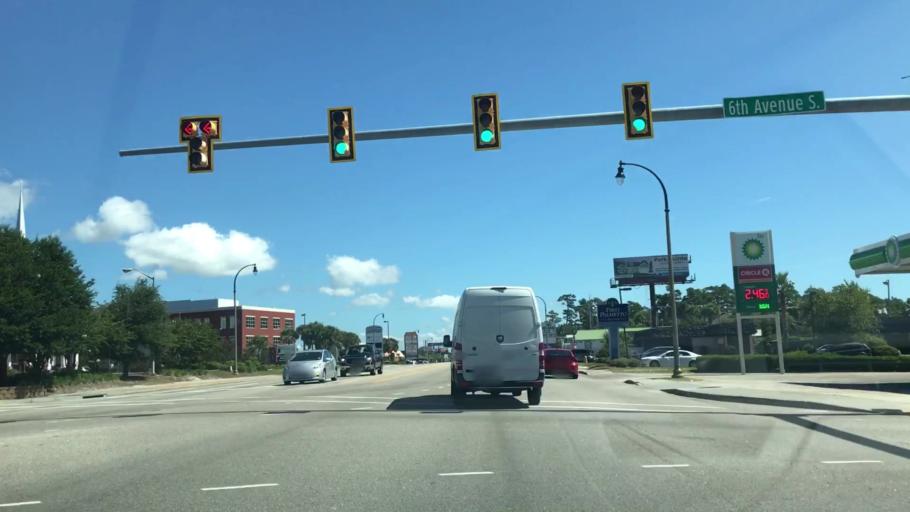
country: US
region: South Carolina
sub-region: Horry County
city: North Myrtle Beach
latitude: 33.8247
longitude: -78.6843
